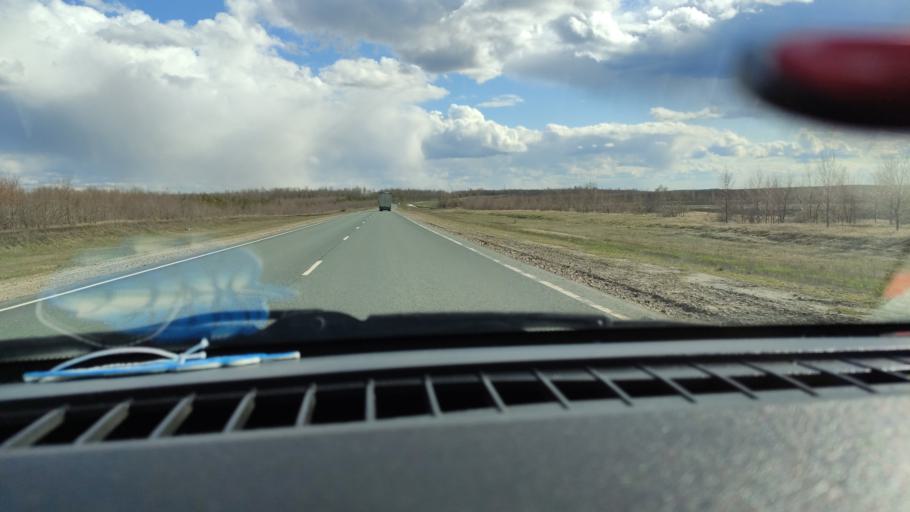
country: RU
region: Saratov
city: Alekseyevka
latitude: 52.2808
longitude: 47.9319
